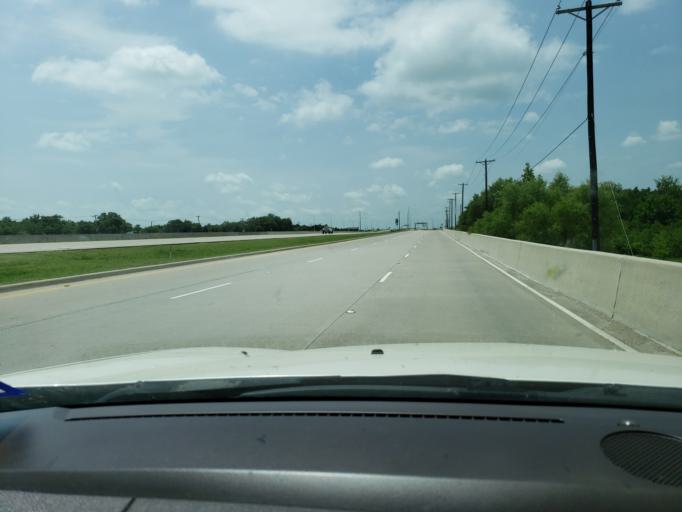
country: US
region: Texas
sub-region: Dallas County
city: Rowlett
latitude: 32.8995
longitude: -96.5565
